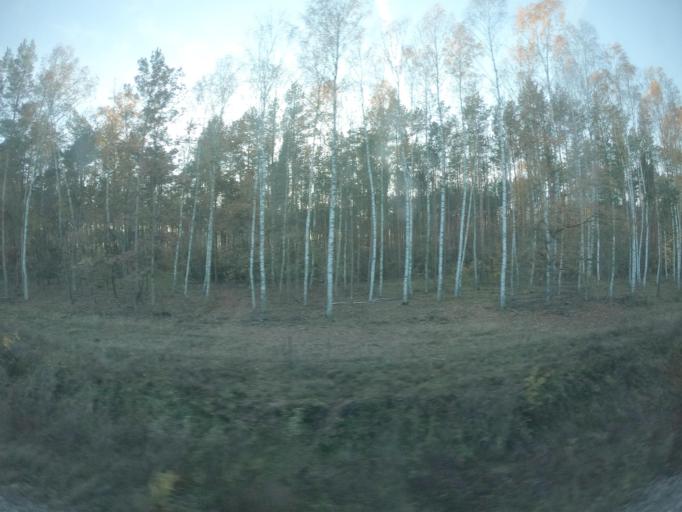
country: PL
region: Lubusz
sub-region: Powiat slubicki
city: Rzepin
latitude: 52.3309
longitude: 14.8385
